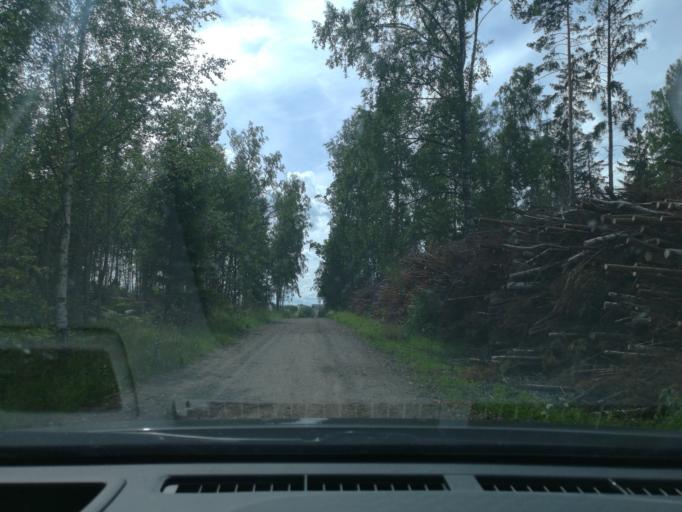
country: SE
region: Stockholm
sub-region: Sigtuna Kommun
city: Marsta
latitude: 59.6084
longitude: 17.8022
